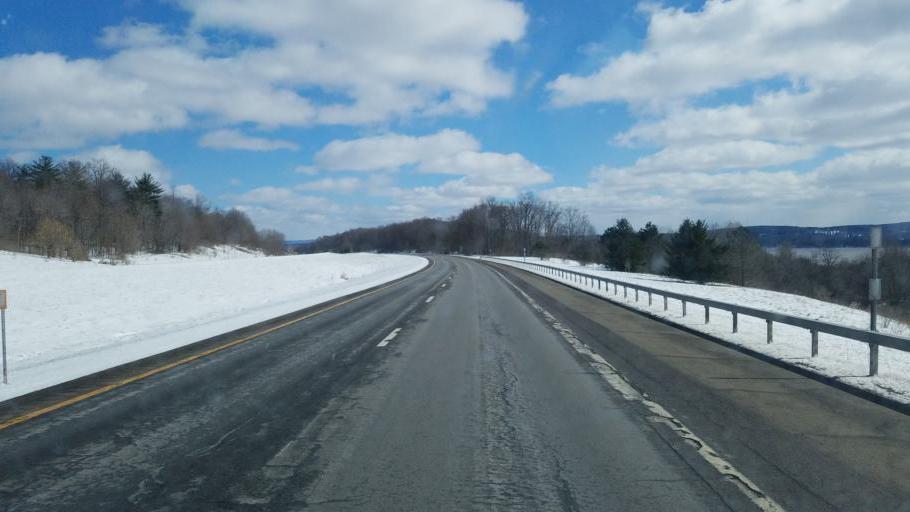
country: US
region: New York
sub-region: Chautauqua County
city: Lakewood
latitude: 42.1315
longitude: -79.3273
